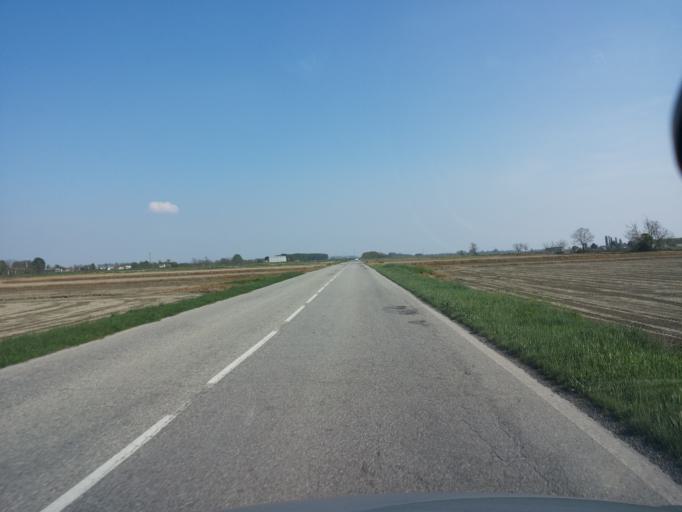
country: IT
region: Lombardy
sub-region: Provincia di Pavia
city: Candia Lomellina
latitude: 45.1937
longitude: 8.5926
